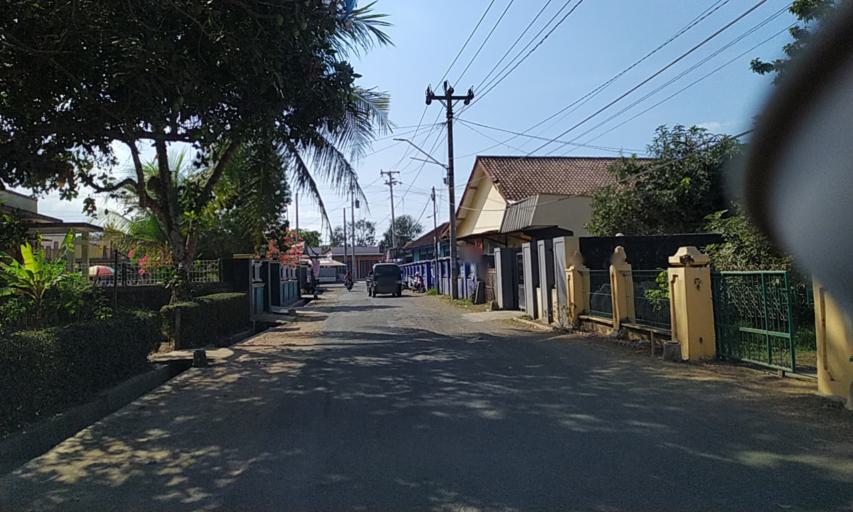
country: ID
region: Central Java
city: Adipala
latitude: -7.6663
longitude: 109.1672
